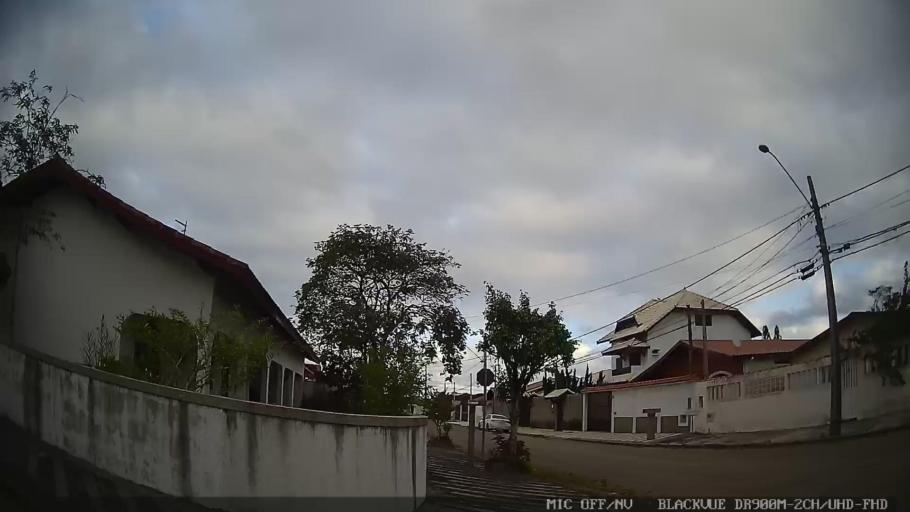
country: BR
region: Sao Paulo
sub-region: Peruibe
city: Peruibe
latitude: -24.3075
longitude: -46.9893
